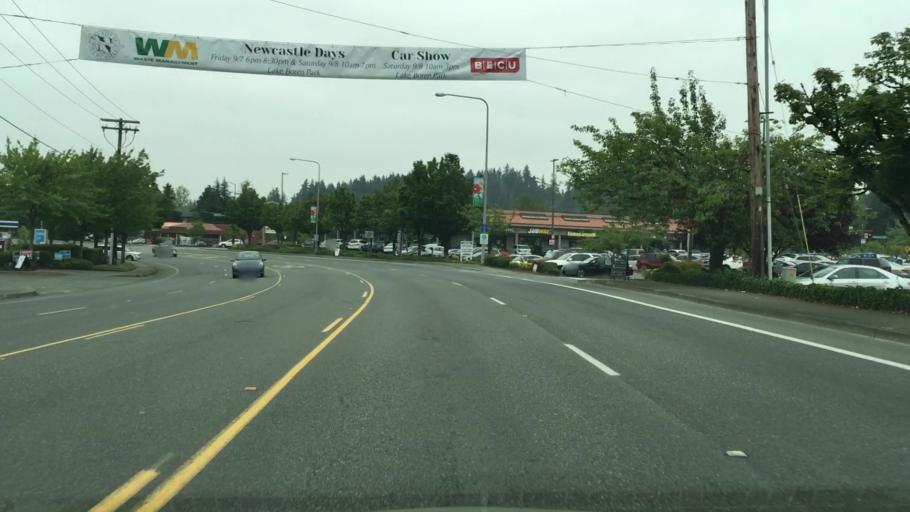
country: US
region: Washington
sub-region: King County
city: Newcastle
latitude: 47.5392
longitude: -122.1660
